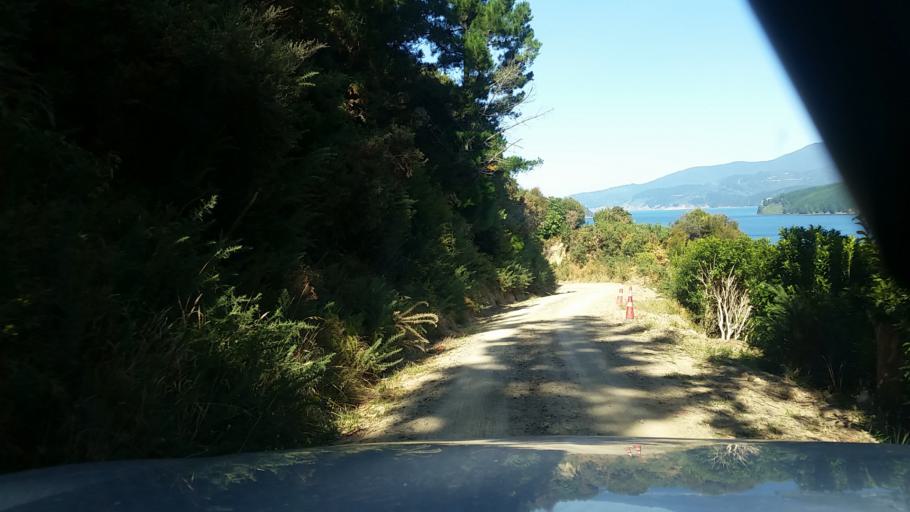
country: NZ
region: Marlborough
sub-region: Marlborough District
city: Picton
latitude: -41.3005
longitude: 174.1787
